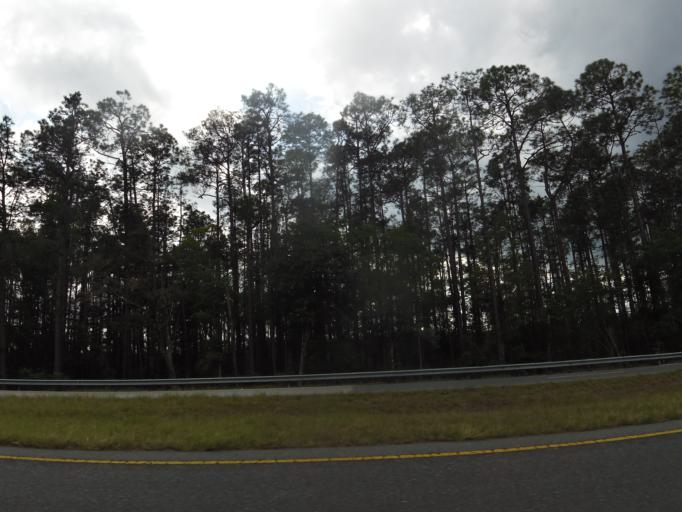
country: US
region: Georgia
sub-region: Charlton County
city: Folkston
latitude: 30.8505
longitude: -81.9303
